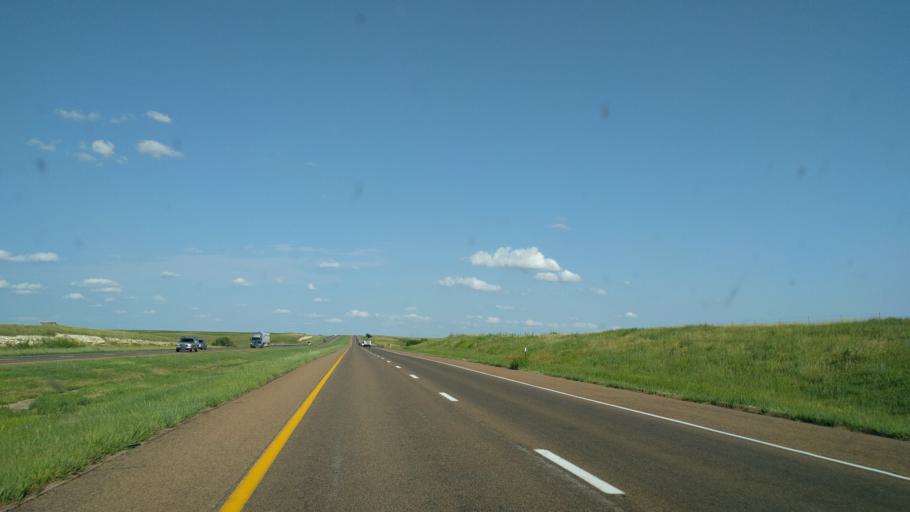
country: US
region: Kansas
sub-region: Ellis County
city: Ellis
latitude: 38.9422
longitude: -99.4978
